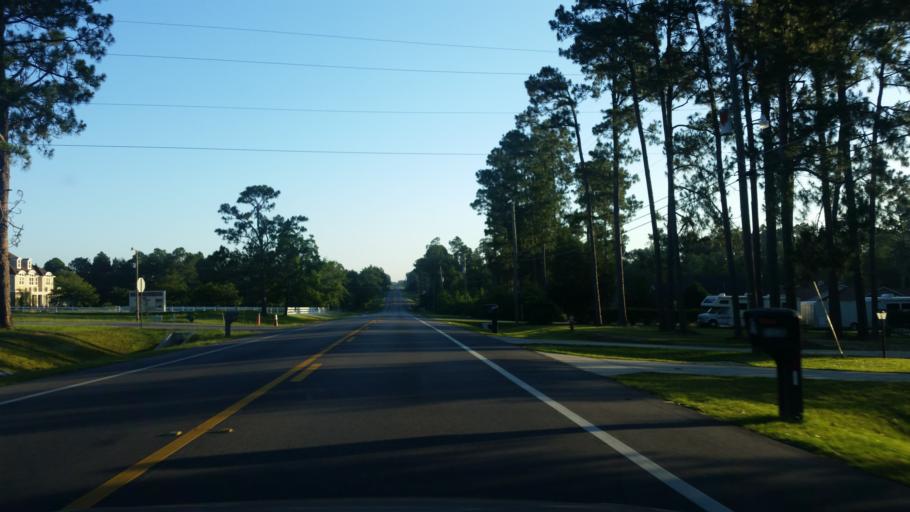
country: US
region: Florida
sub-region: Escambia County
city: Gonzalez
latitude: 30.5674
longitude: -87.3287
